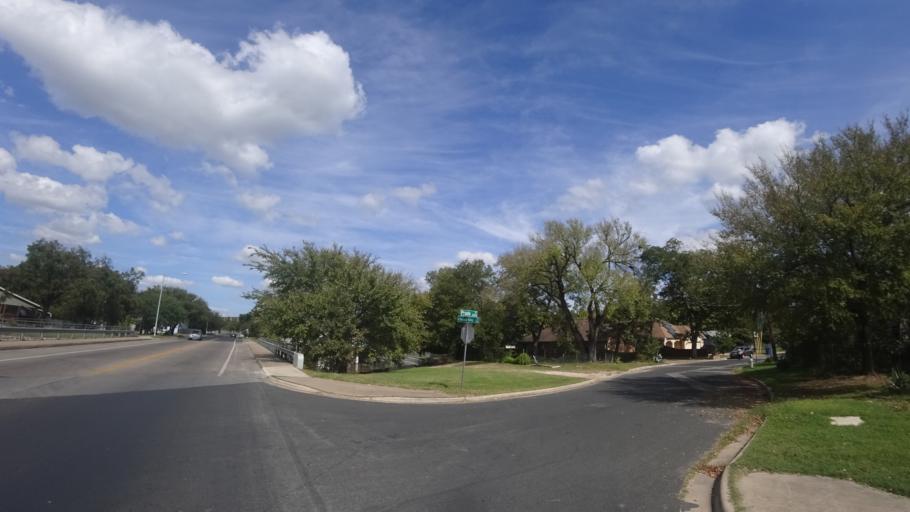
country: US
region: Texas
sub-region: Travis County
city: Austin
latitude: 30.2618
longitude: -97.7088
